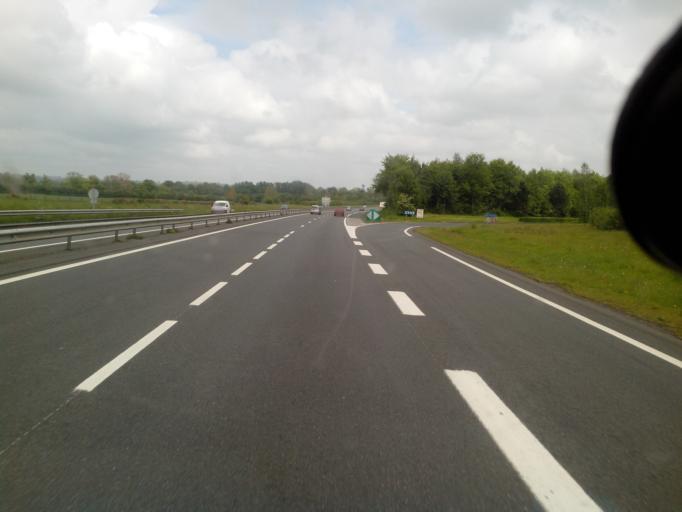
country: FR
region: Lower Normandy
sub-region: Departement du Calvados
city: Cahagnes
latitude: 49.0476
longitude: -0.7790
